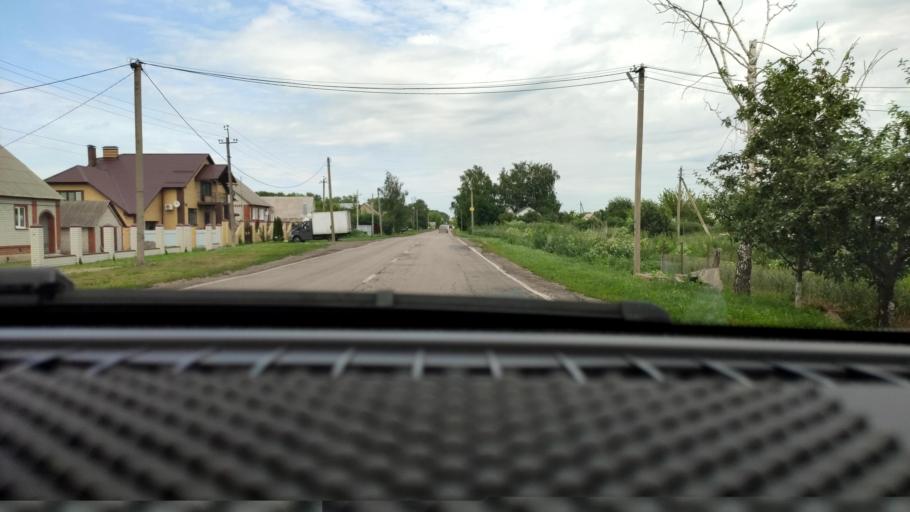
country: RU
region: Voronezj
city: Panino
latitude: 51.6534
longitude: 40.1180
